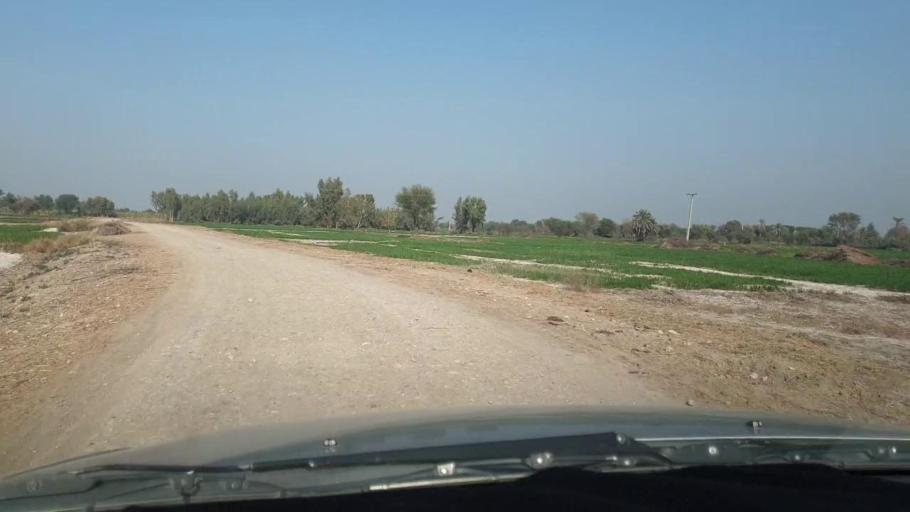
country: PK
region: Sindh
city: Mirpur Mathelo
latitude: 27.9169
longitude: 69.5565
